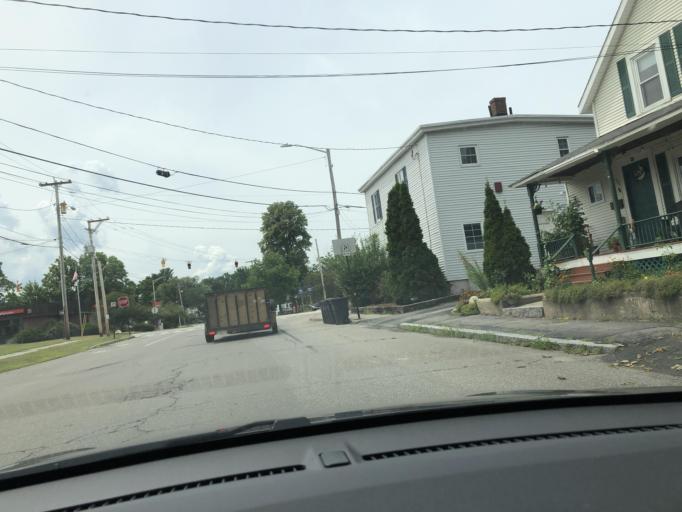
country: US
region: New Hampshire
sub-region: Merrimack County
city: Concord
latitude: 43.1939
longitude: -71.5381
